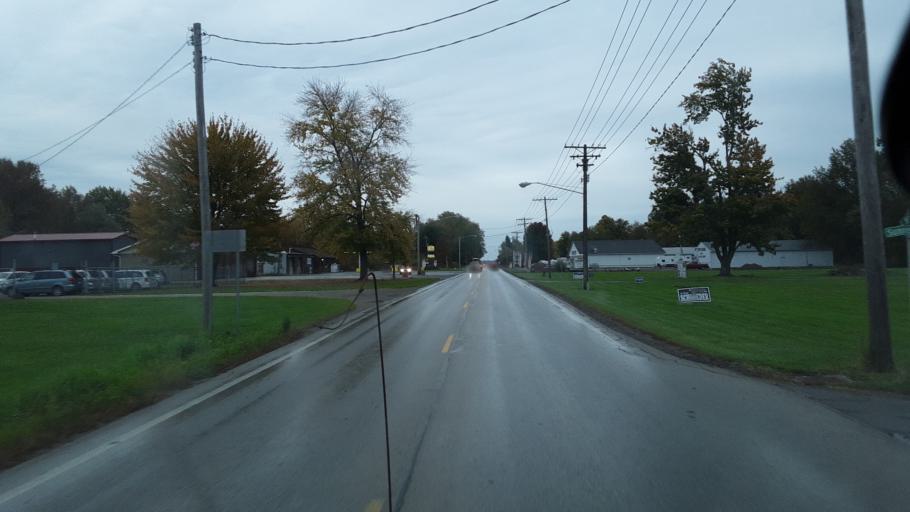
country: US
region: Ohio
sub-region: Ashtabula County
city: Orwell
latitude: 41.5351
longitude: -80.8464
